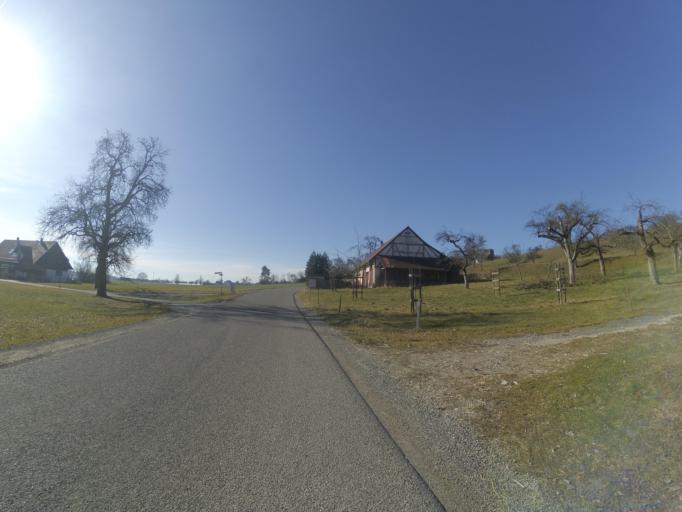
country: DE
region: Baden-Wuerttemberg
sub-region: Tuebingen Region
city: Wolpertswende
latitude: 47.9053
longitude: 9.6206
